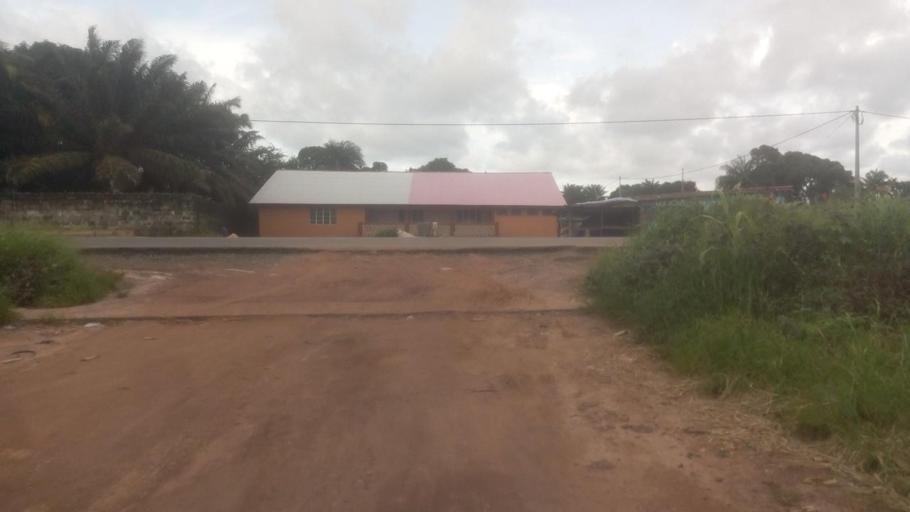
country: SL
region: Northern Province
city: Masoyila
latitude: 8.6075
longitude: -13.1844
